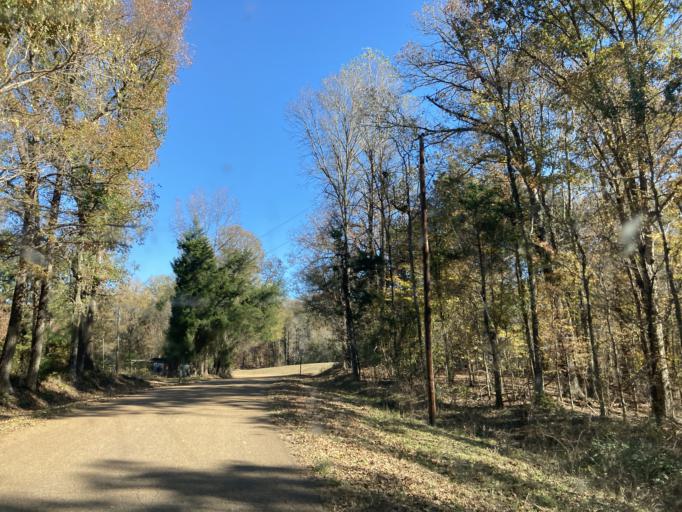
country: US
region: Mississippi
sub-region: Hinds County
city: Lynchburg
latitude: 32.5528
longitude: -90.5939
